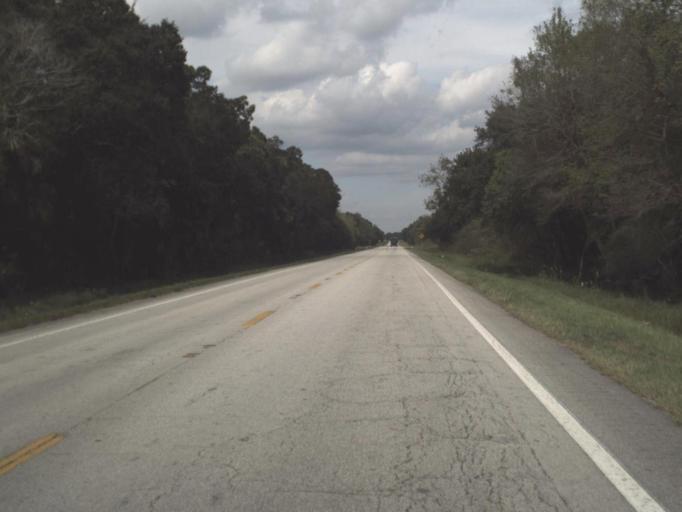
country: US
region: Florida
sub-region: Okeechobee County
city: Cypress Quarters
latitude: 27.3609
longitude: -80.8197
